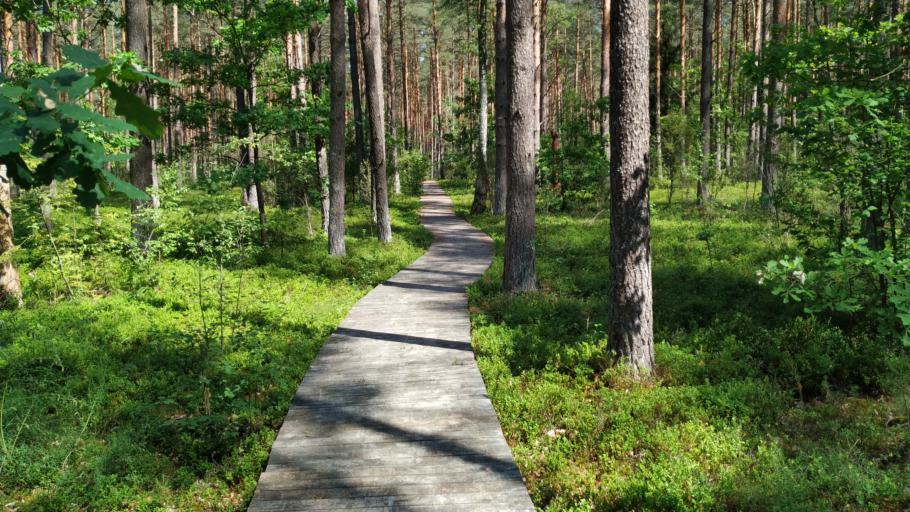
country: LT
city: Nemencine
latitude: 54.8075
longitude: 25.3975
